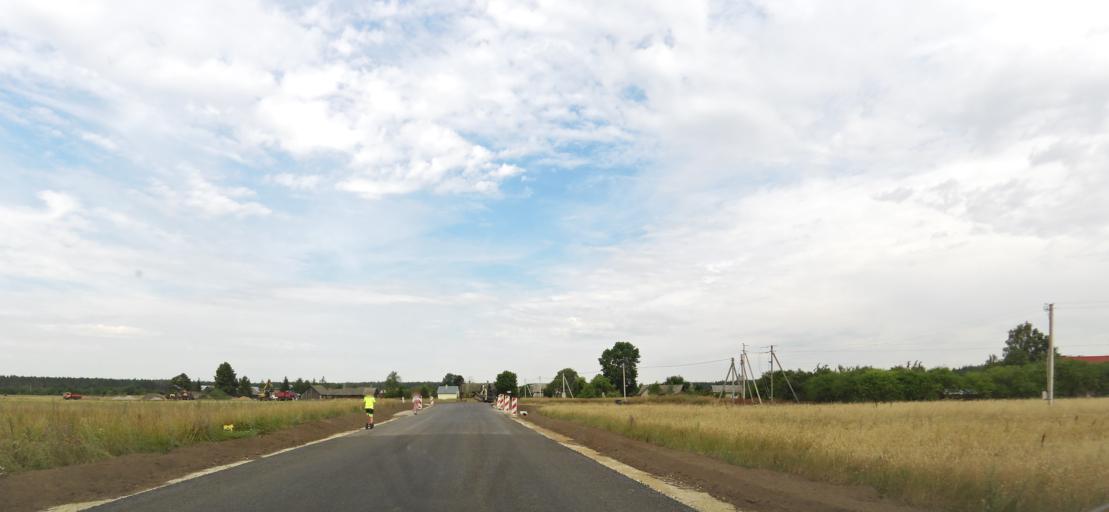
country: LT
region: Vilnius County
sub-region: Trakai
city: Rudiskes
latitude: 54.4624
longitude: 24.9774
